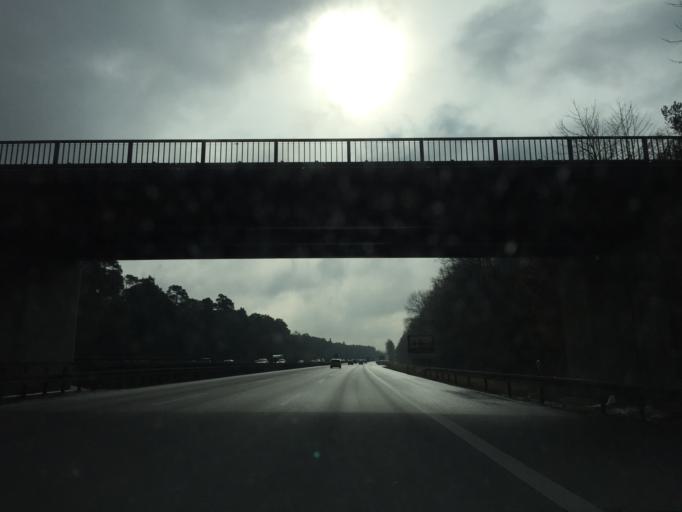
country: DE
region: Bavaria
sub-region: Upper Bavaria
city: Reichertshofen
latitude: 48.6709
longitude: 11.5073
